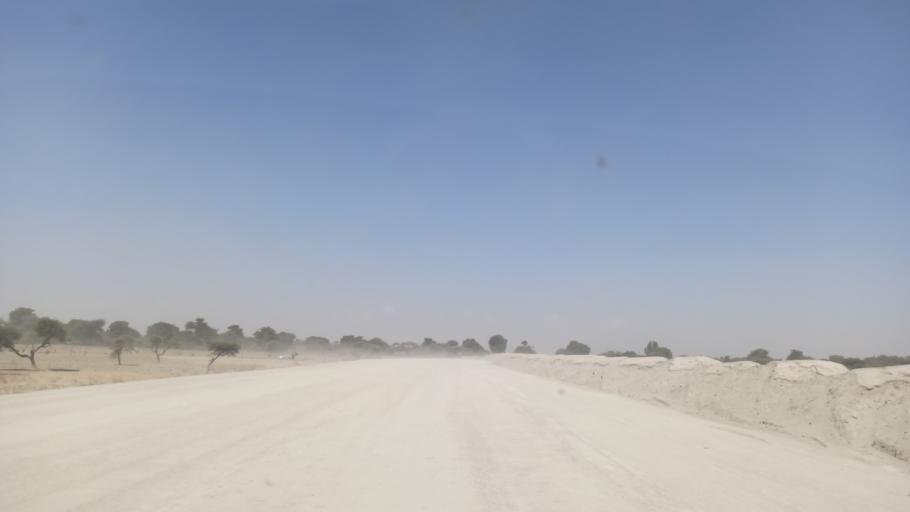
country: ET
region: Oromiya
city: Ziway
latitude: 7.6996
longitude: 38.6423
